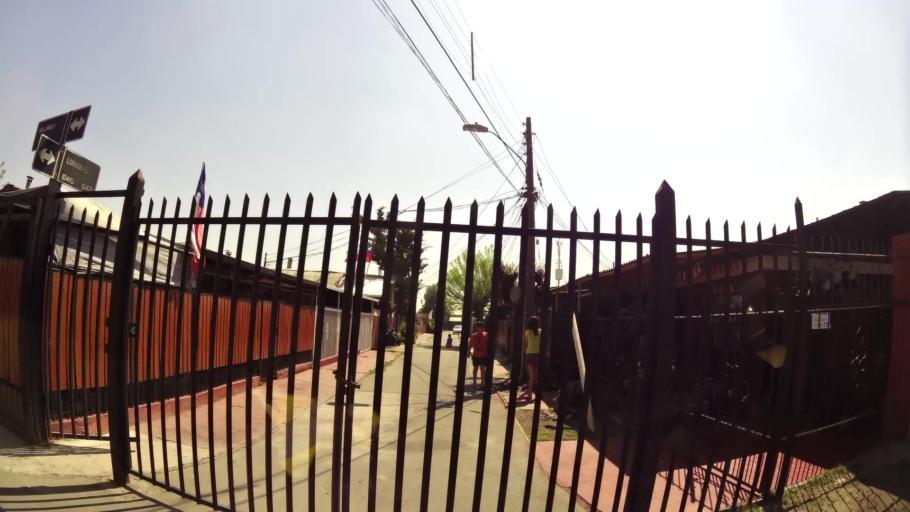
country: CL
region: Santiago Metropolitan
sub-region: Provincia de Santiago
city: La Pintana
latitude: -33.5556
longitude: -70.6032
